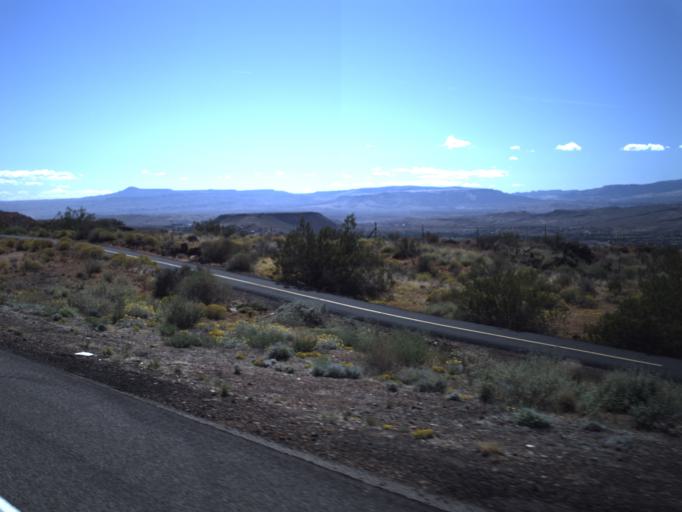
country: US
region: Utah
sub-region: Washington County
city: Santa Clara
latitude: 37.1654
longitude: -113.6128
